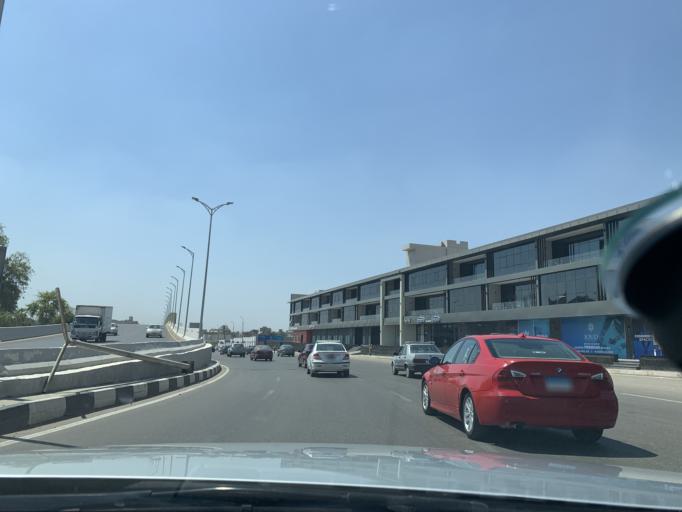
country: EG
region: Muhafazat al Qahirah
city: Cairo
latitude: 30.0919
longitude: 31.3482
